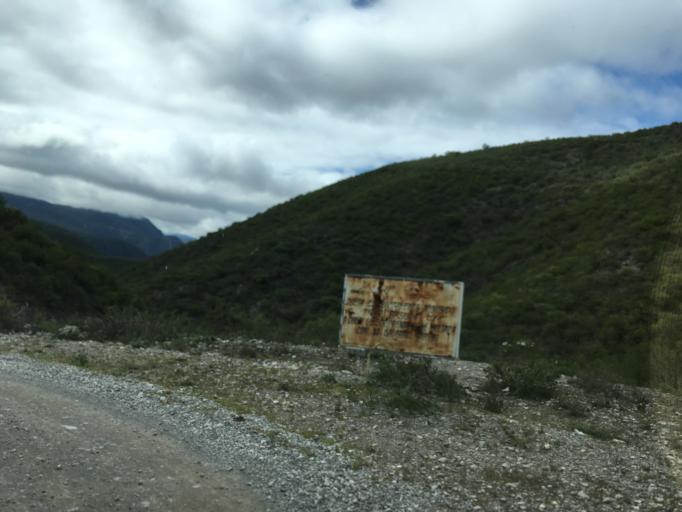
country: MX
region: Hidalgo
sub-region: Metztitlan
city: Fontezuelas
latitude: 20.6238
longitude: -98.8779
